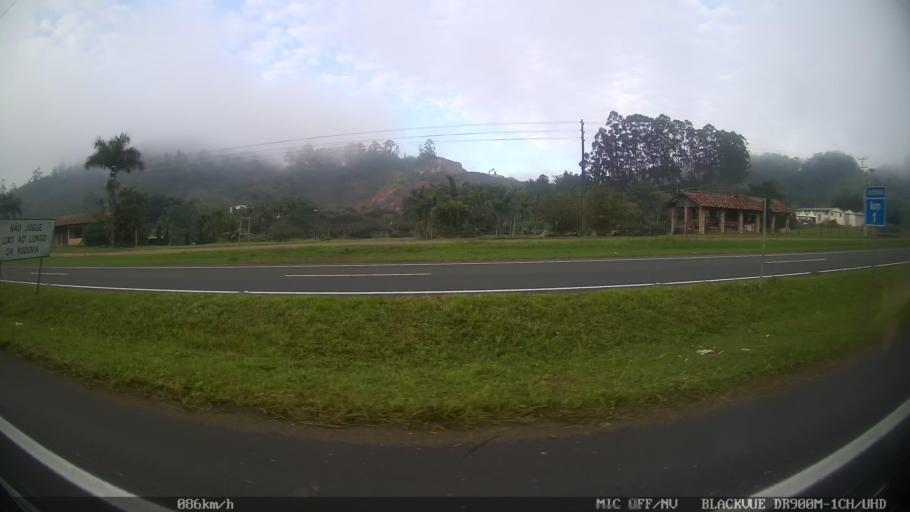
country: BR
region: Santa Catarina
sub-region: Penha
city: Penha
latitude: -26.8098
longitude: -48.6696
